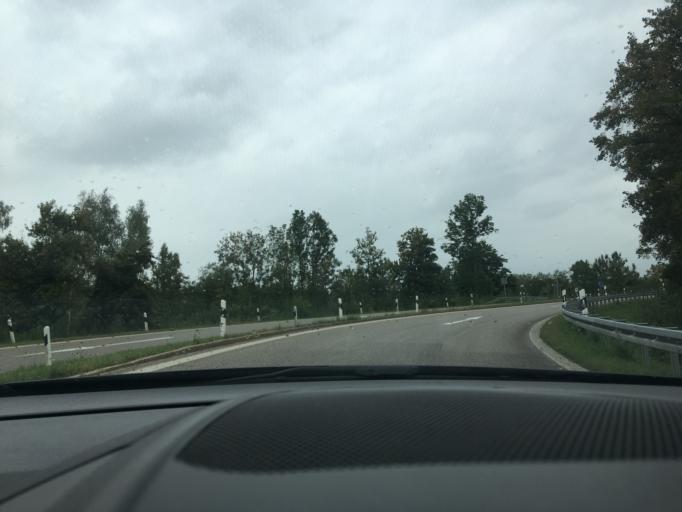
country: DE
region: Bavaria
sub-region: Swabia
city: Heimertingen
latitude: 48.0358
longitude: 10.1336
